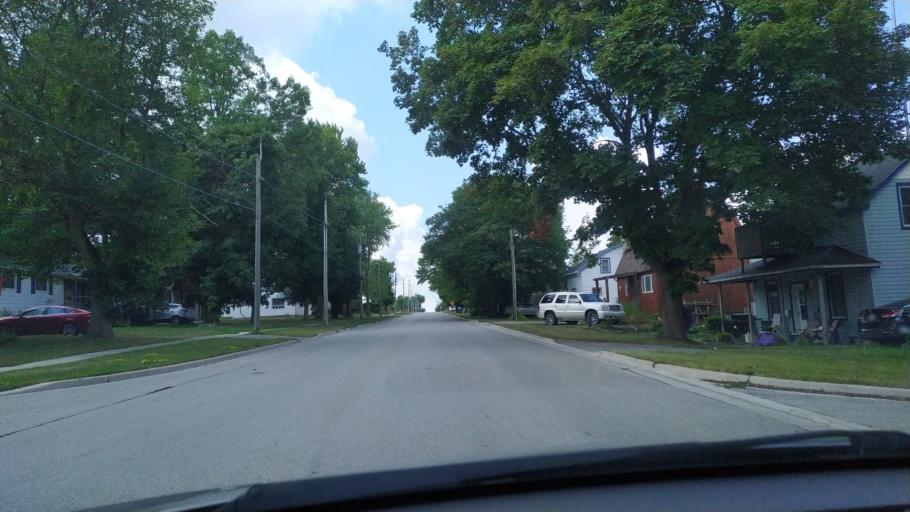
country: CA
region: Ontario
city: Huron East
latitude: 43.4636
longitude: -81.1938
